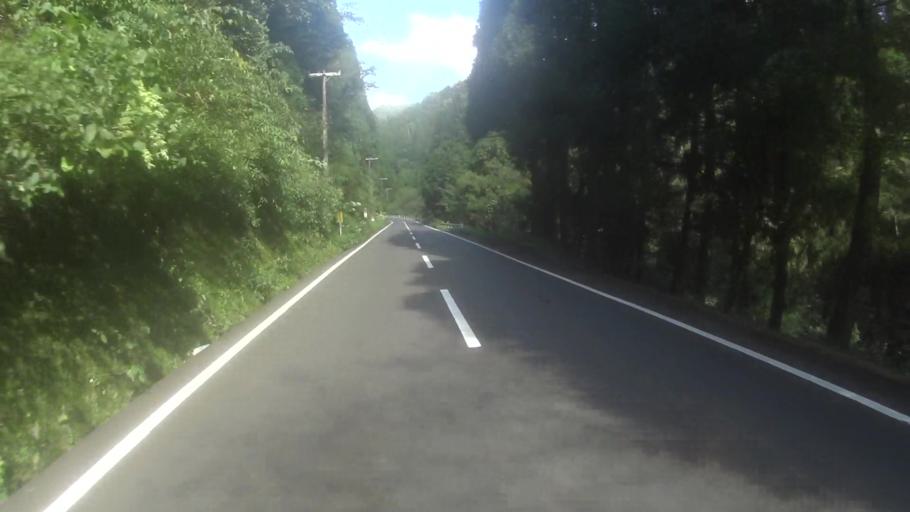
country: JP
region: Kyoto
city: Miyazu
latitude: 35.6425
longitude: 135.1296
